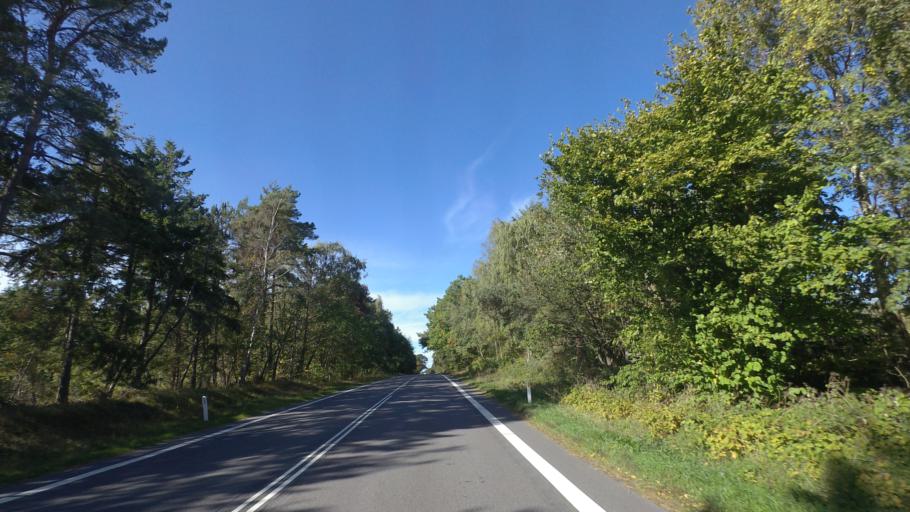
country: DK
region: Capital Region
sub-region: Bornholm Kommune
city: Ronne
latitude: 55.0823
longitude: 14.7523
